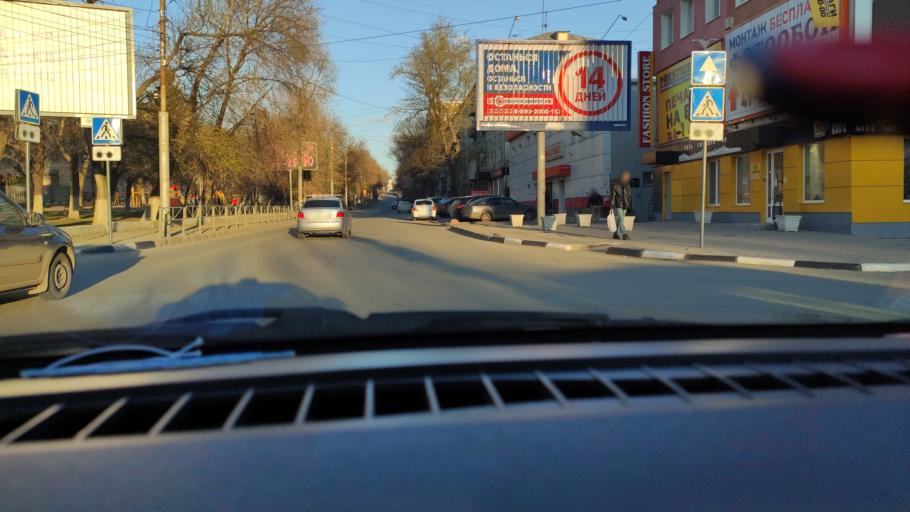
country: RU
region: Saratov
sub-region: Saratovskiy Rayon
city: Saratov
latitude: 51.5389
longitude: 46.0453
